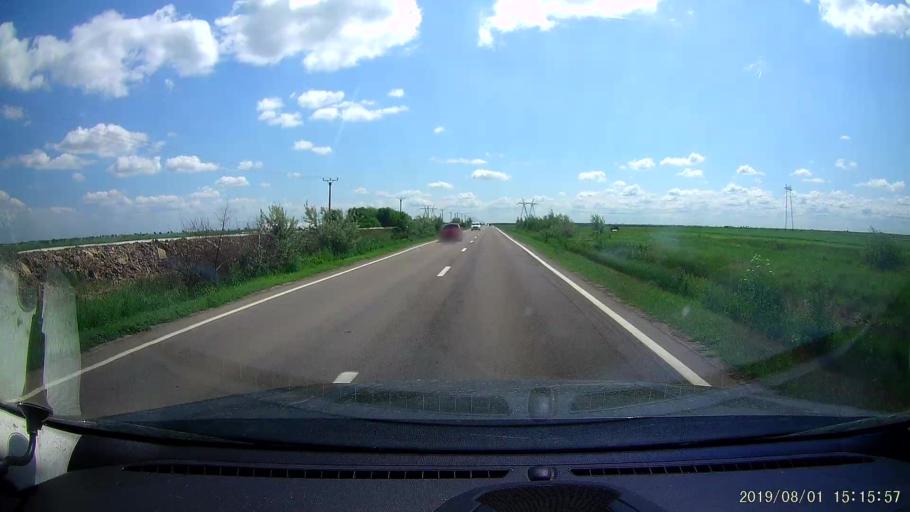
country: RO
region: Braila
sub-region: Comuna Tichilesti
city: Tichilesti
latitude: 45.1565
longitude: 27.8613
